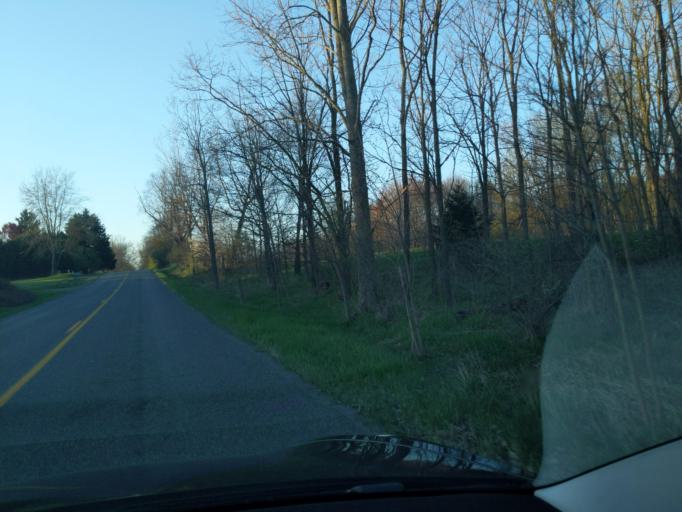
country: US
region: Michigan
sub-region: Ingham County
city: Stockbridge
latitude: 42.4860
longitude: -84.2399
